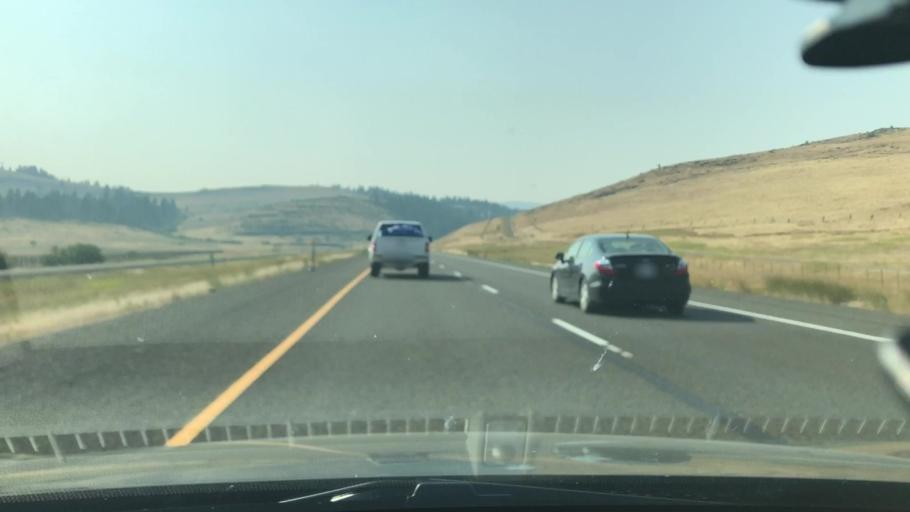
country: US
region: Oregon
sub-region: Union County
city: Union
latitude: 45.1715
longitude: -117.9706
